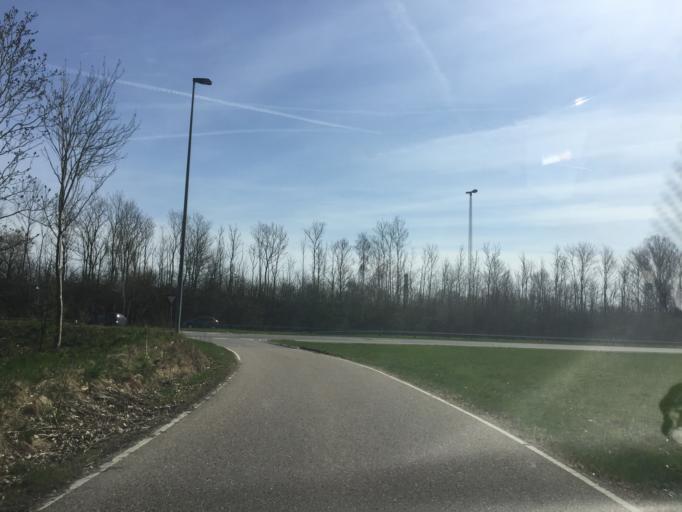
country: DK
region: Capital Region
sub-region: Hoje-Taastrup Kommune
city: Taastrup
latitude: 55.6407
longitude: 12.2801
